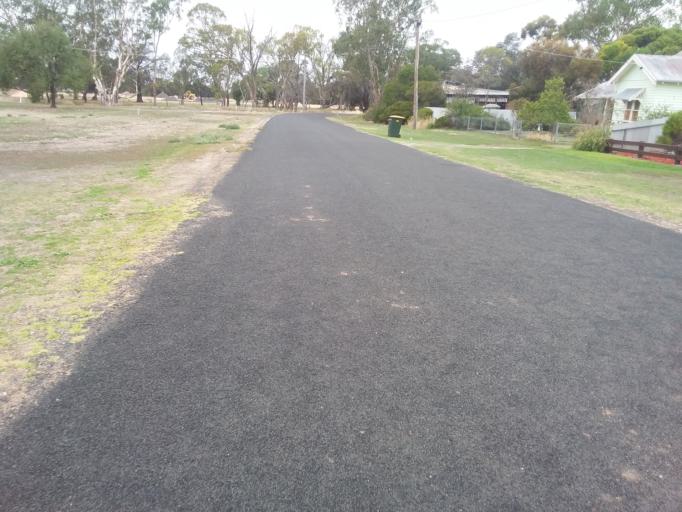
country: AU
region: Victoria
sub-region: Horsham
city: Horsham
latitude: -36.7406
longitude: 141.9386
